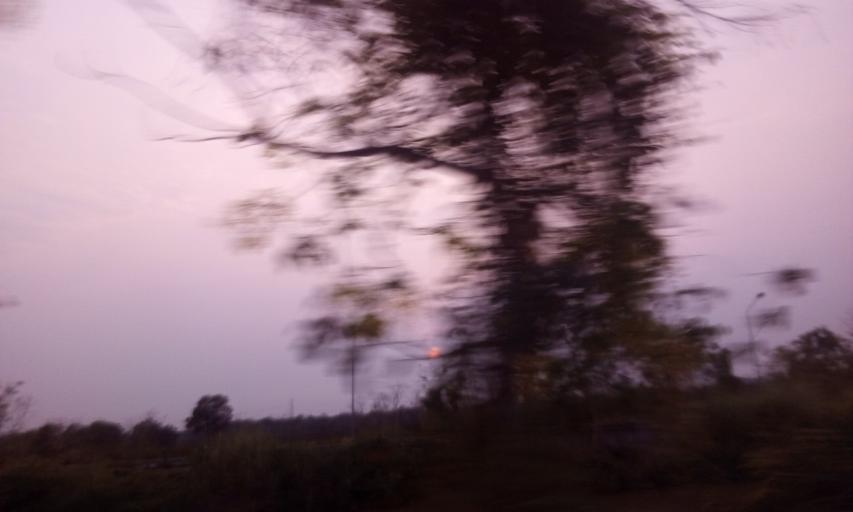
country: TH
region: Pathum Thani
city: Nong Suea
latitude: 14.0648
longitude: 100.8927
